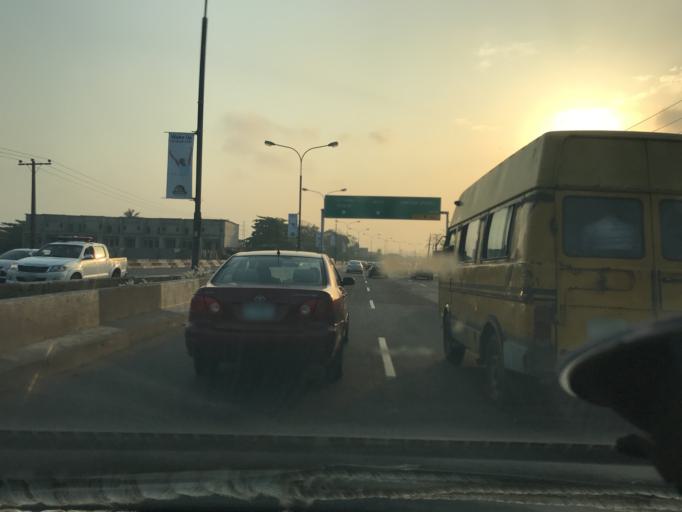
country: NG
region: Lagos
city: Lagos
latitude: 6.4584
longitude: 3.4031
